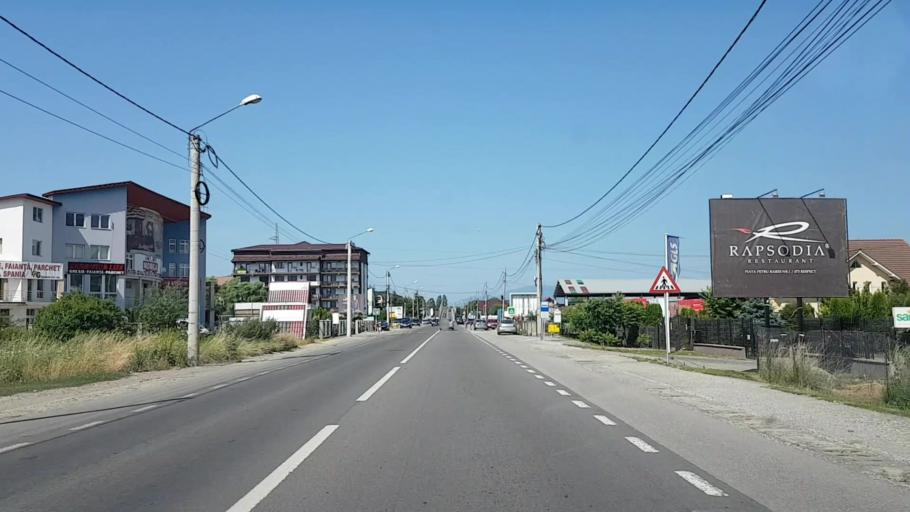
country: RO
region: Bistrita-Nasaud
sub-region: Municipiul Bistrita
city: Viisoara
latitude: 47.1118
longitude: 24.4600
